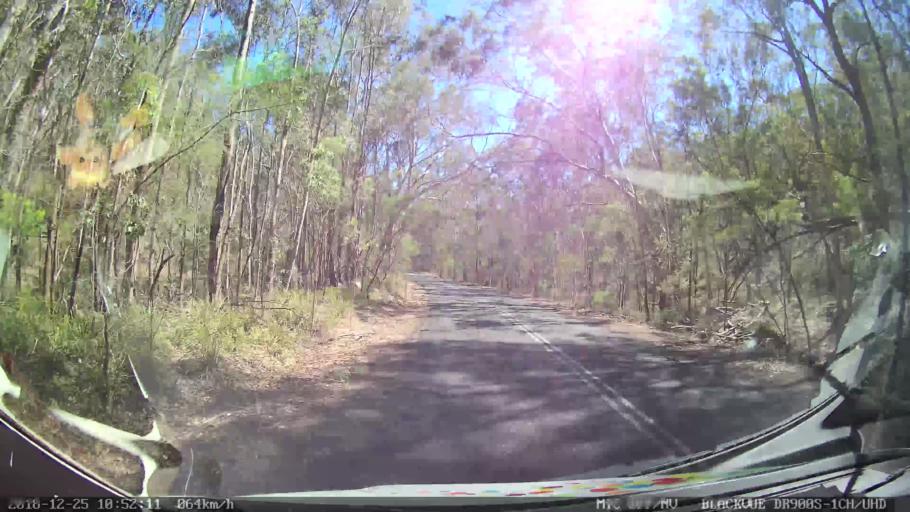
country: AU
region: New South Wales
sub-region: Upper Hunter Shire
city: Merriwa
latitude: -32.4310
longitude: 150.2735
